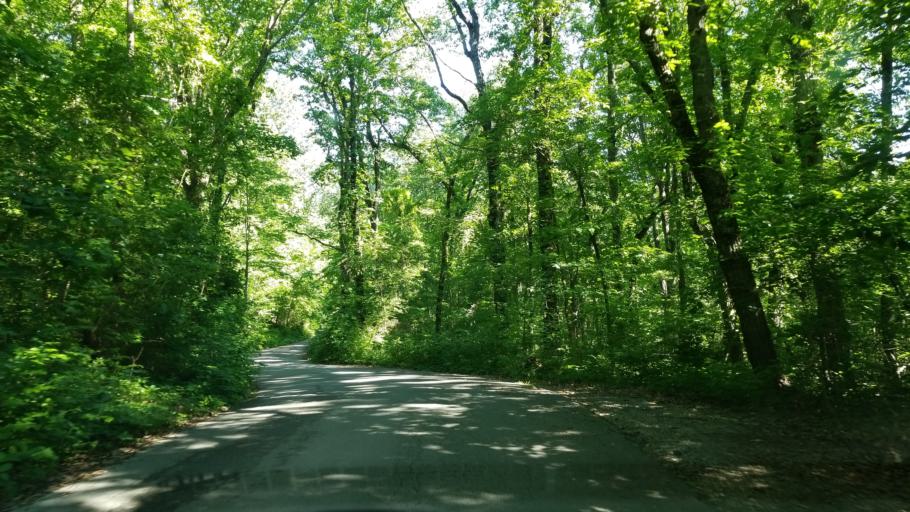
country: US
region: Tennessee
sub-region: Hamilton County
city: Lookout Mountain
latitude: 35.0096
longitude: -85.3393
